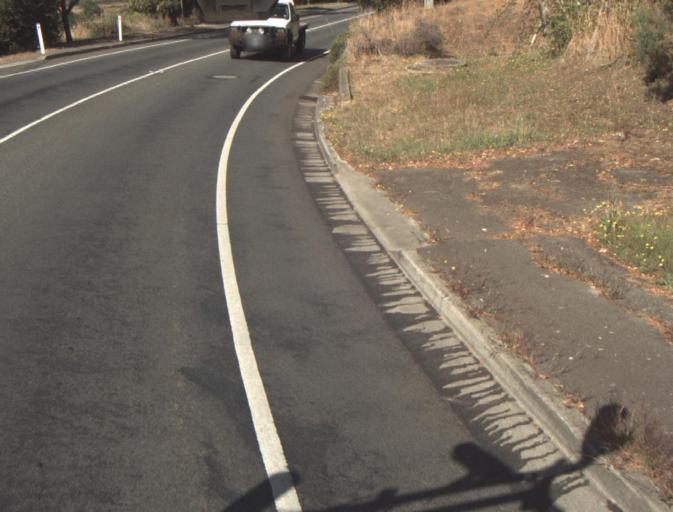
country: AU
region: Tasmania
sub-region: Launceston
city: Newstead
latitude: -41.4292
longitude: 147.1759
